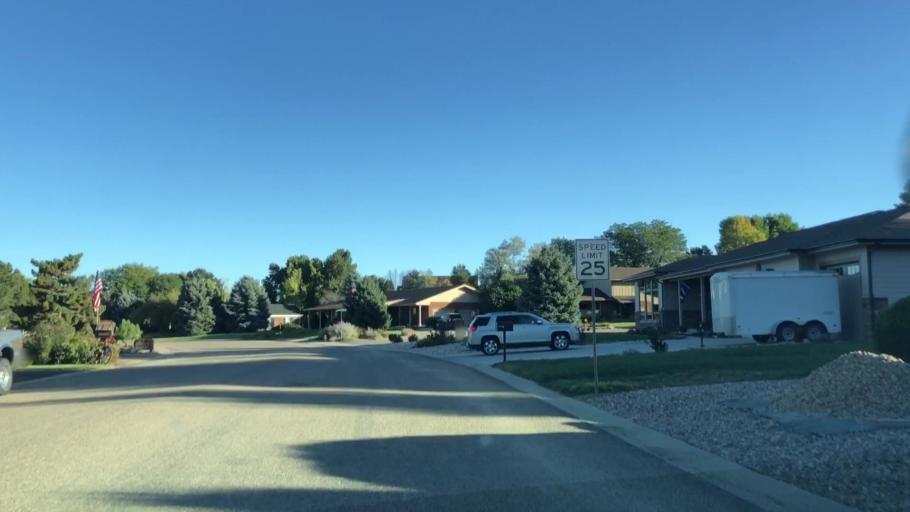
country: US
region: Colorado
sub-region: Larimer County
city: Loveland
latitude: 40.4291
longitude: -105.0221
